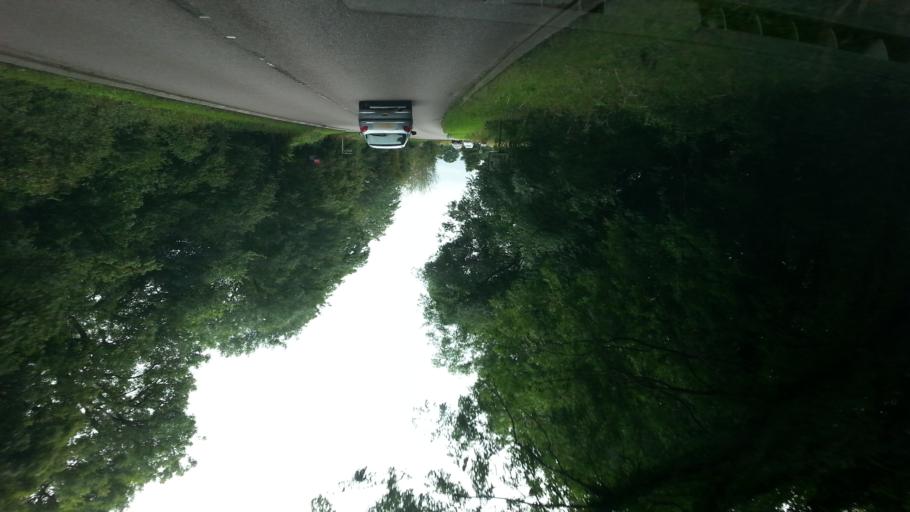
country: GB
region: England
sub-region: Wiltshire
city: Trowbridge
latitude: 51.3174
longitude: -2.1656
